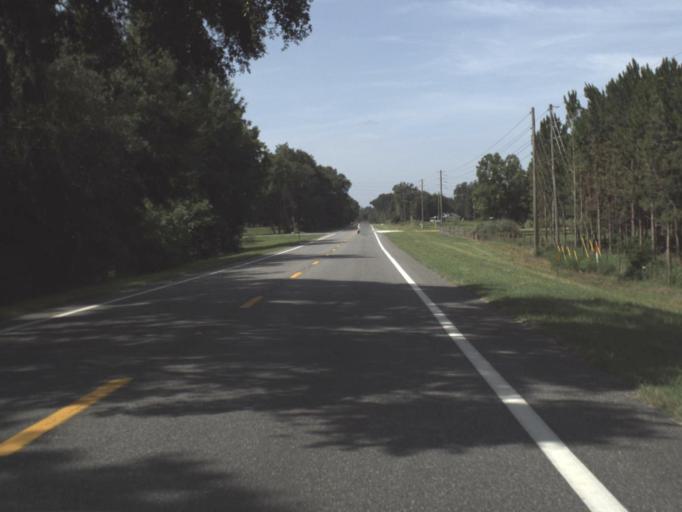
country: US
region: Florida
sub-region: Lafayette County
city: Mayo
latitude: 30.1458
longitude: -83.1649
